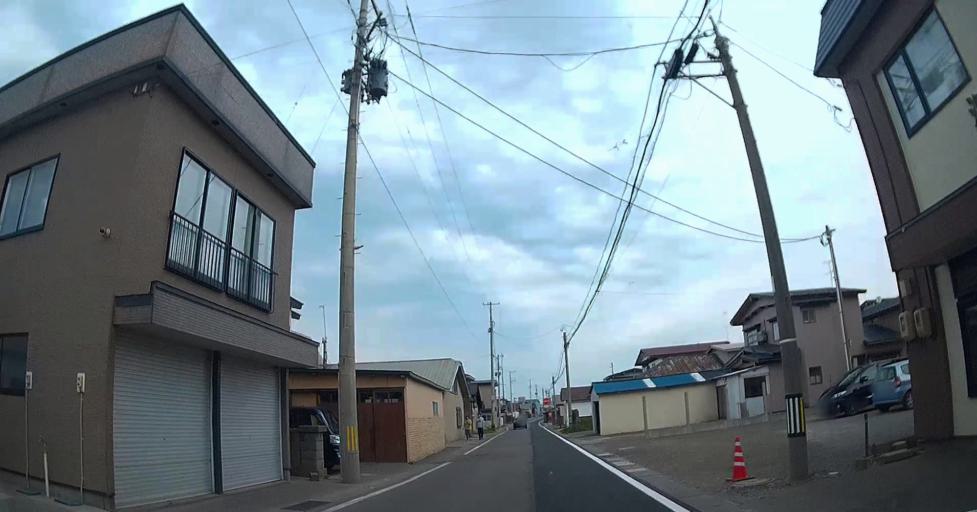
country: JP
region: Aomori
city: Shimokizukuri
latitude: 41.0263
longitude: 140.3258
